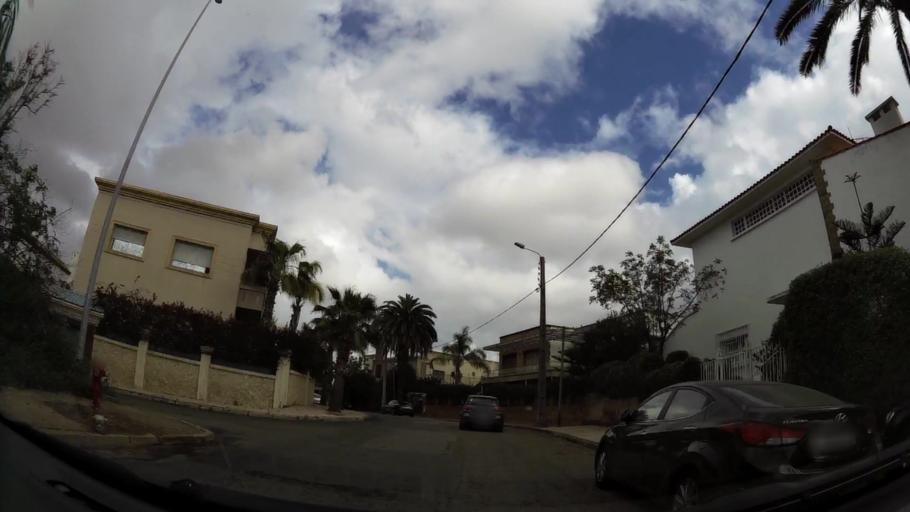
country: MA
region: Grand Casablanca
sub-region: Casablanca
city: Casablanca
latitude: 33.5511
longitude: -7.6164
